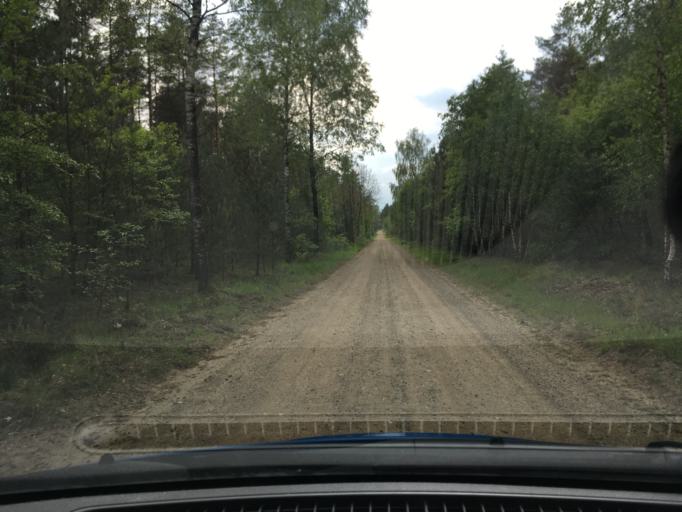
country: DE
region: Lower Saxony
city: Eimke
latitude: 52.9614
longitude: 10.2316
